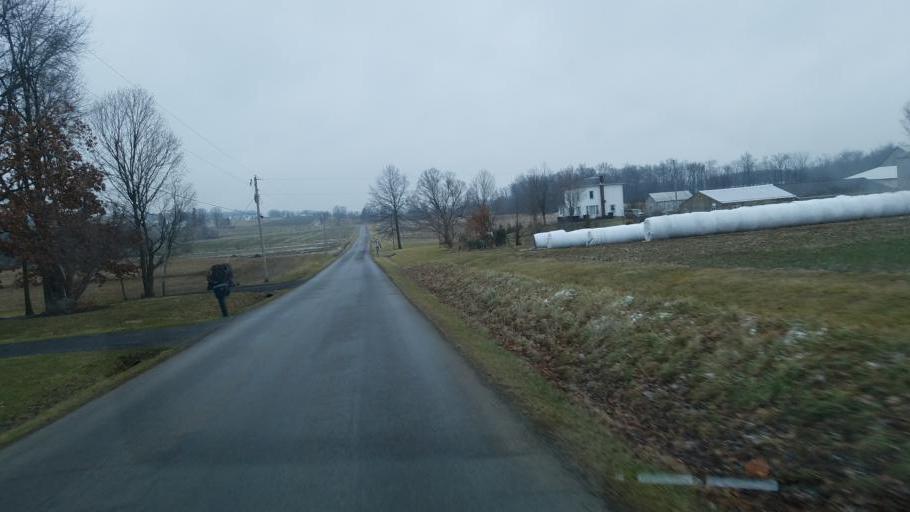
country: US
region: Ohio
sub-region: Wayne County
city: Apple Creek
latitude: 40.7200
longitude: -81.8624
